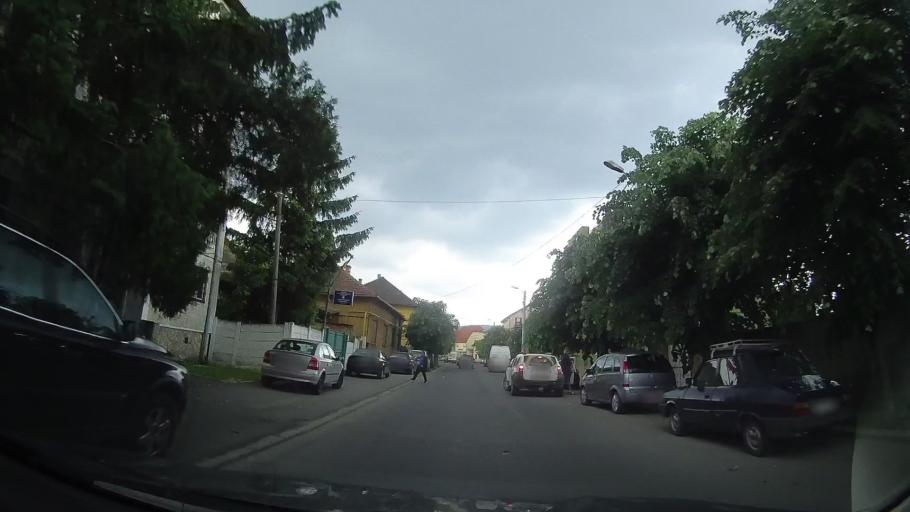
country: RO
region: Caras-Severin
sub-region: Municipiul Caransebes
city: Caransebes
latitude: 45.4130
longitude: 22.2123
